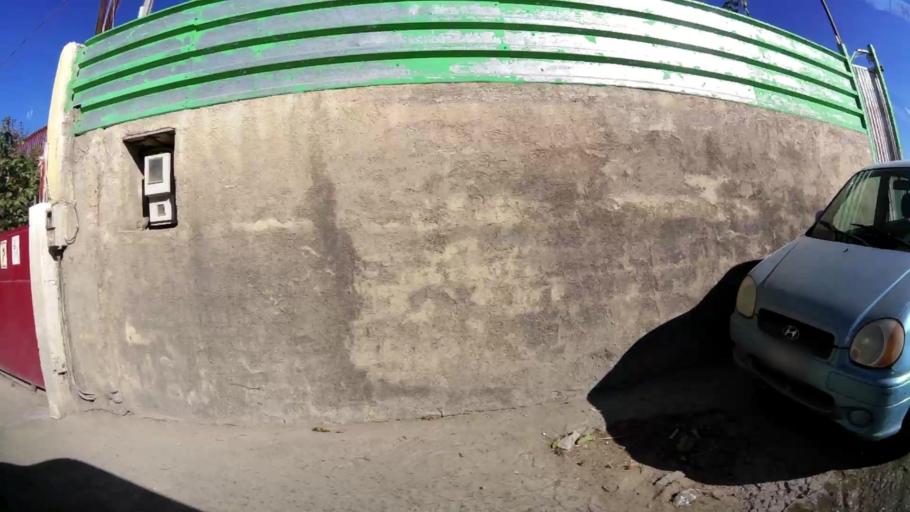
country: GR
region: Attica
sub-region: Nomarchia Athinas
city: Metamorfosi
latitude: 38.0792
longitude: 23.7539
